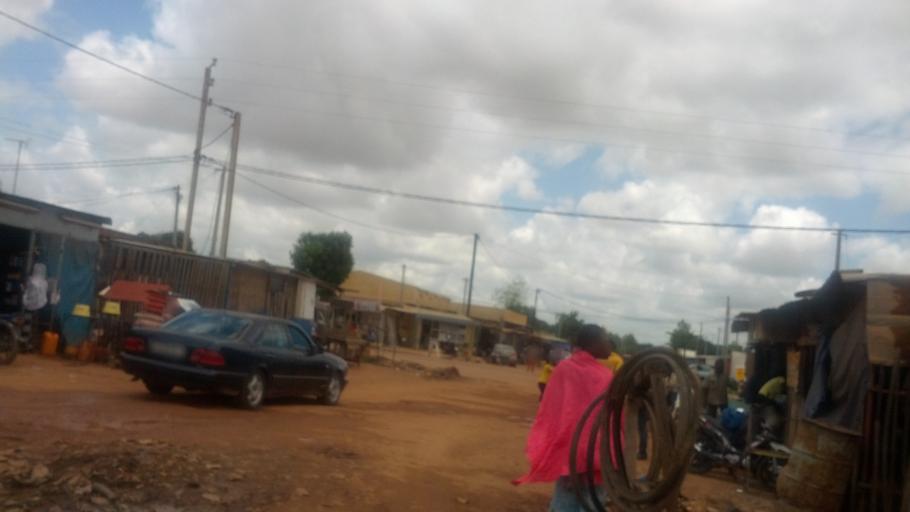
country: BF
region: Centre
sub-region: Kadiogo Province
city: Ouagadougou
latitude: 12.3405
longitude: -1.5081
